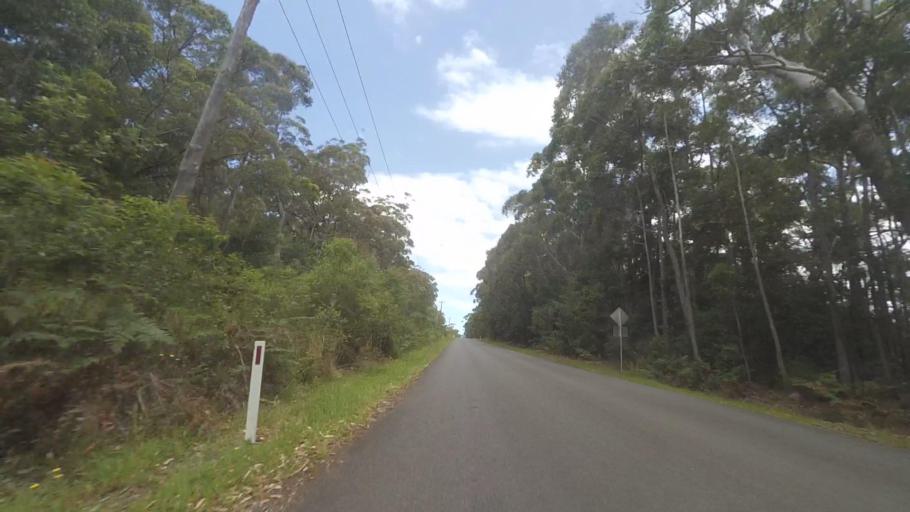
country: AU
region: New South Wales
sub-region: Shoalhaven Shire
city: Milton
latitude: -35.3851
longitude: 150.3656
